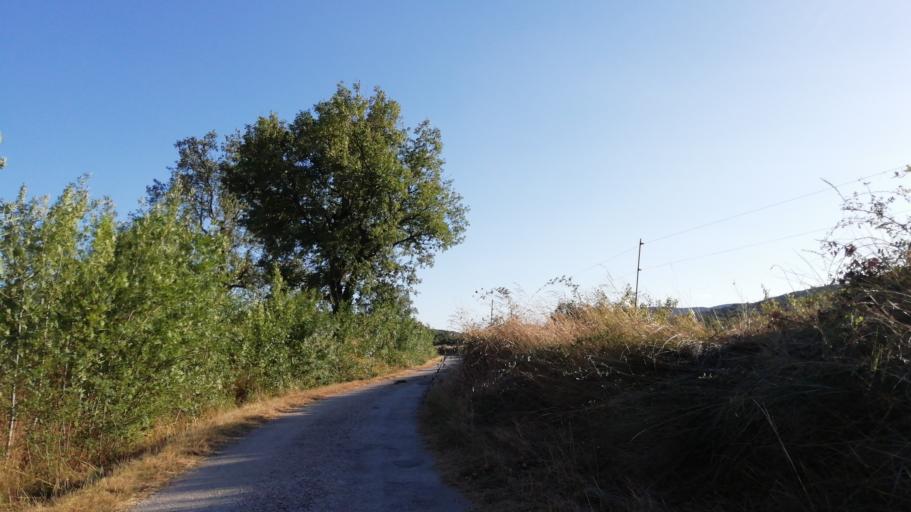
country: FR
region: Languedoc-Roussillon
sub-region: Departement de l'Herault
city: Saint-Martin-de-Londres
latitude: 43.7827
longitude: 3.7297
